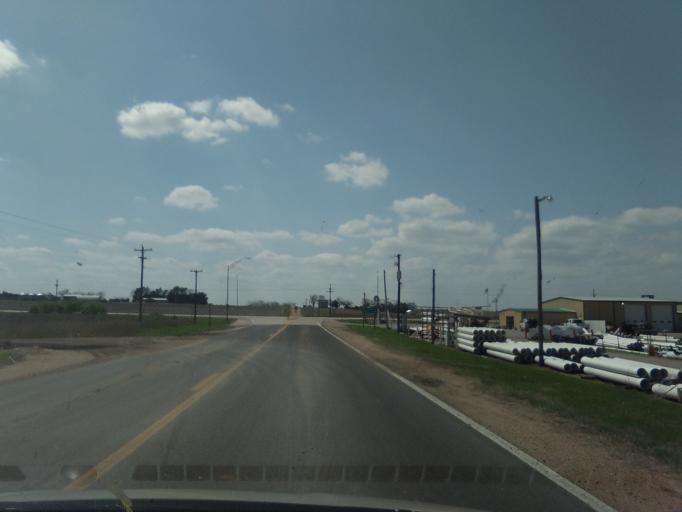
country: US
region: Nebraska
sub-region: Thayer County
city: Hebron
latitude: 40.2490
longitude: -97.5745
